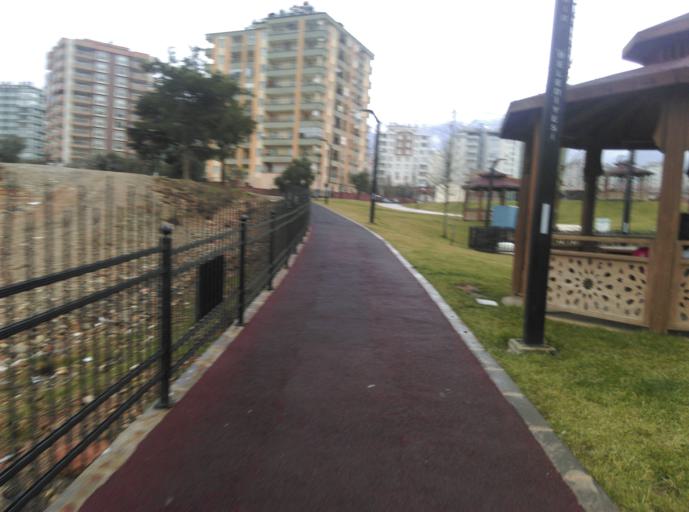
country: TR
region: Kahramanmaras
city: Kahramanmaras
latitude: 37.5812
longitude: 36.8893
